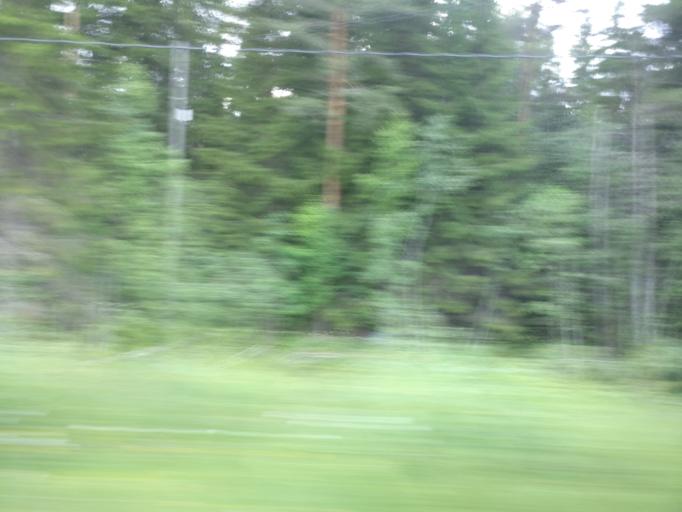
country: FI
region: Northern Savo
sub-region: Koillis-Savo
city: Juankoski
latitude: 62.9433
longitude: 28.2137
